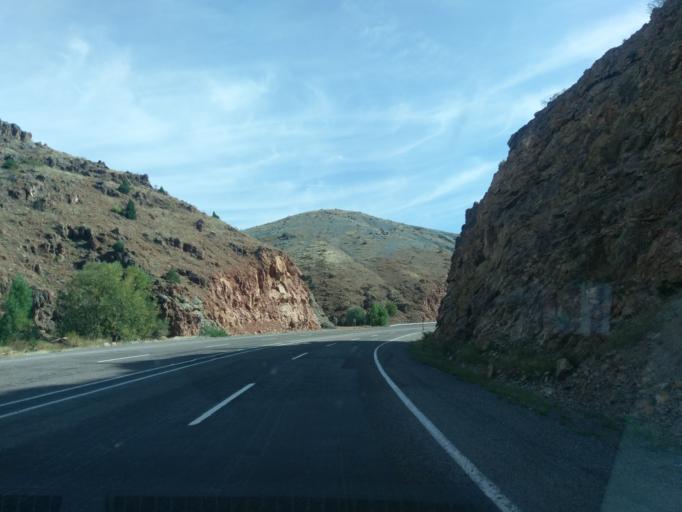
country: TR
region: Sivas
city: Imranli
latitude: 39.8594
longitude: 38.3172
